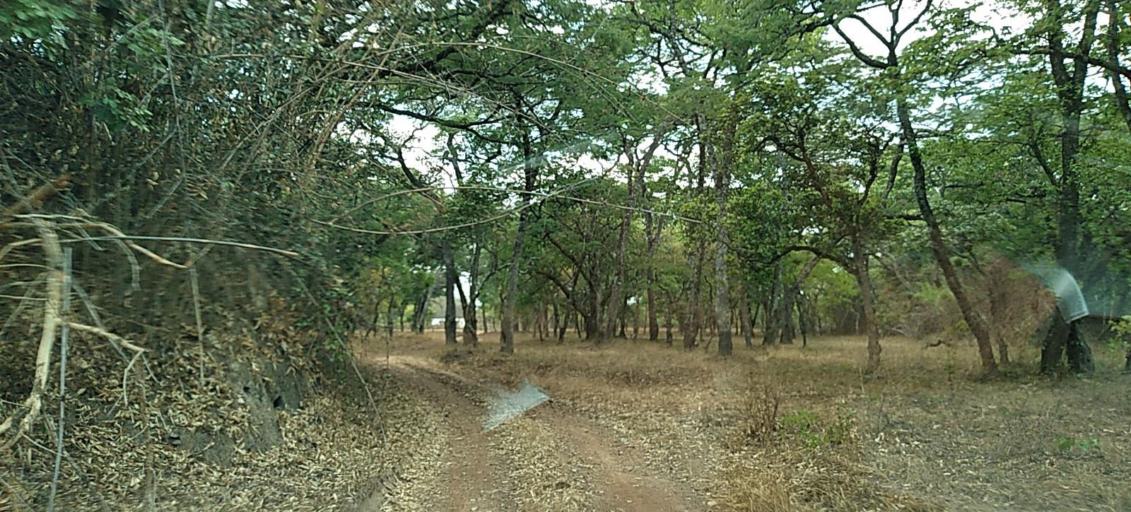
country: ZM
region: Copperbelt
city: Chililabombwe
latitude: -12.4787
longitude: 27.7007
